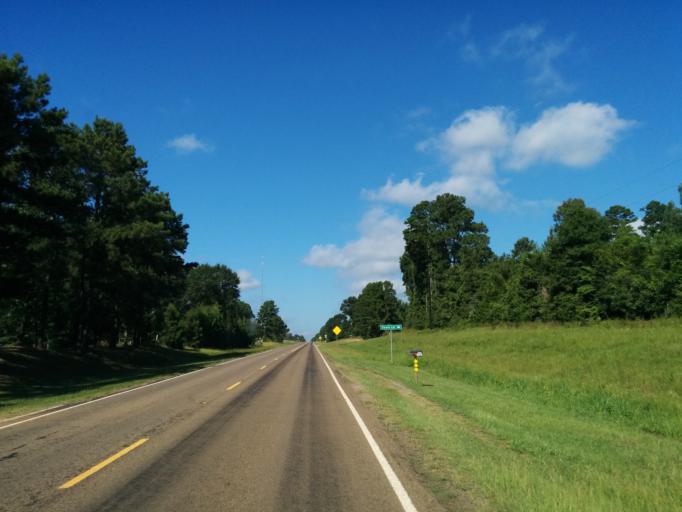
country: US
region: Texas
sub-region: Sabine County
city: Milam
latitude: 31.4230
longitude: -93.9679
